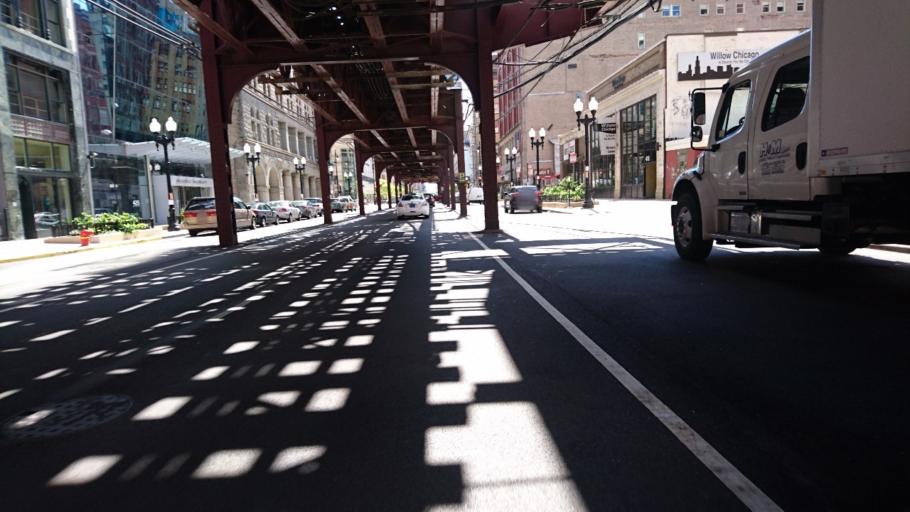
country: US
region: Illinois
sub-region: Cook County
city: Chicago
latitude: 41.8769
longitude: -87.6262
